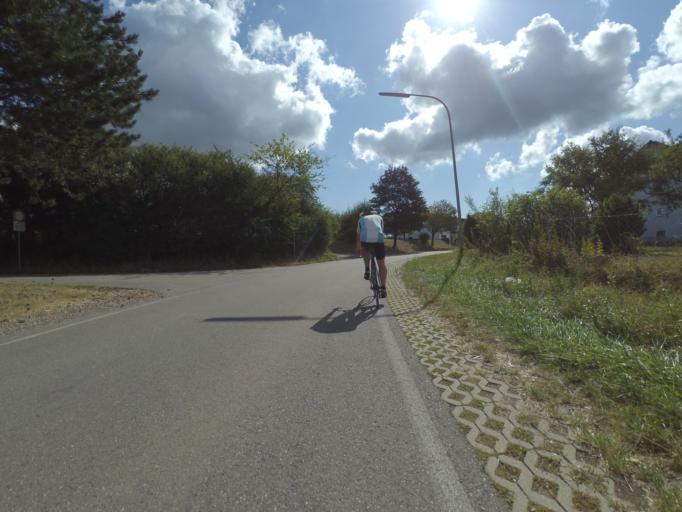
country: DE
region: Rheinland-Pfalz
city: Kirf
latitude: 49.5295
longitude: 6.4825
